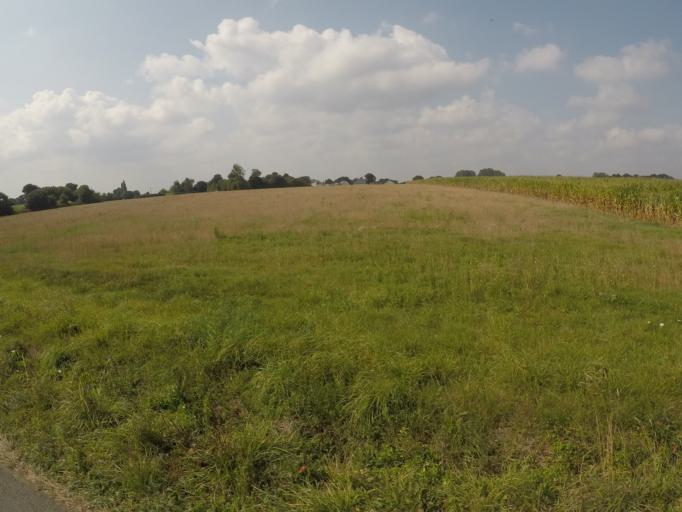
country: FR
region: Brittany
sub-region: Departement des Cotes-d'Armor
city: Tremuson
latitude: 48.5309
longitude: -2.8931
